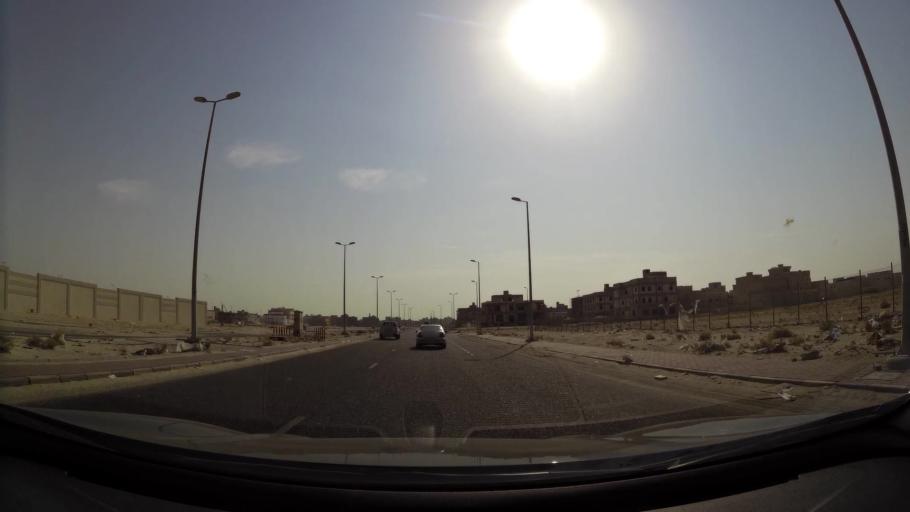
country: KW
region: Al Ahmadi
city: Al Wafrah
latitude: 28.7885
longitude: 48.0431
